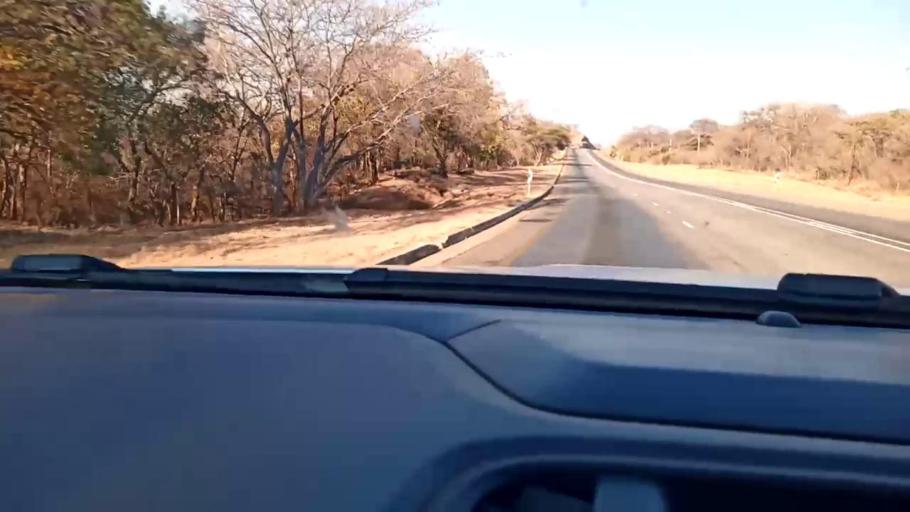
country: ZA
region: Limpopo
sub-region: Mopani District Municipality
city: Duiwelskloof
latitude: -23.6367
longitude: 30.1439
